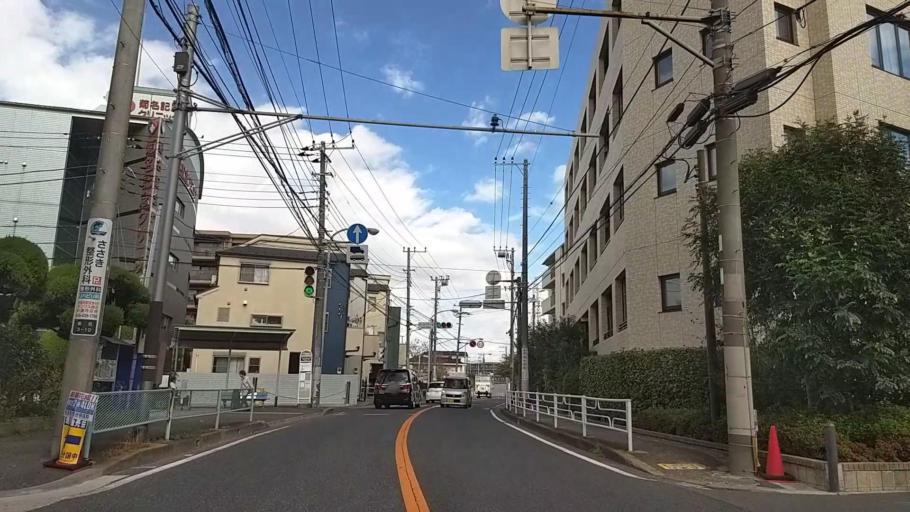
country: JP
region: Kanagawa
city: Yokohama
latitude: 35.5055
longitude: 139.6386
